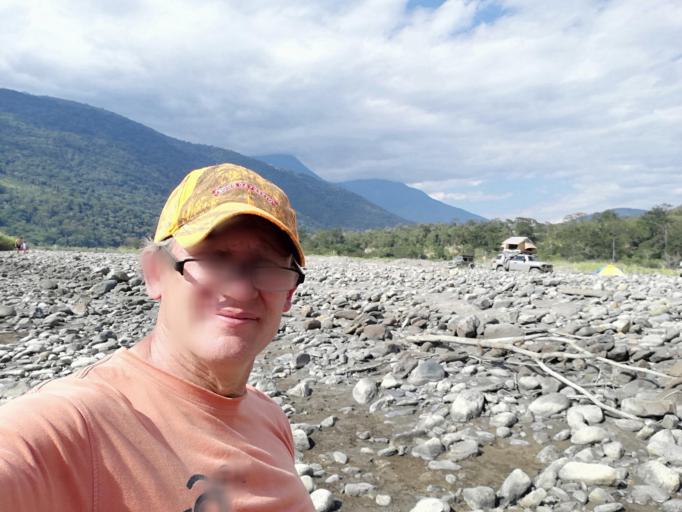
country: BO
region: La Paz
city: Quime
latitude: -16.4708
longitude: -66.7865
